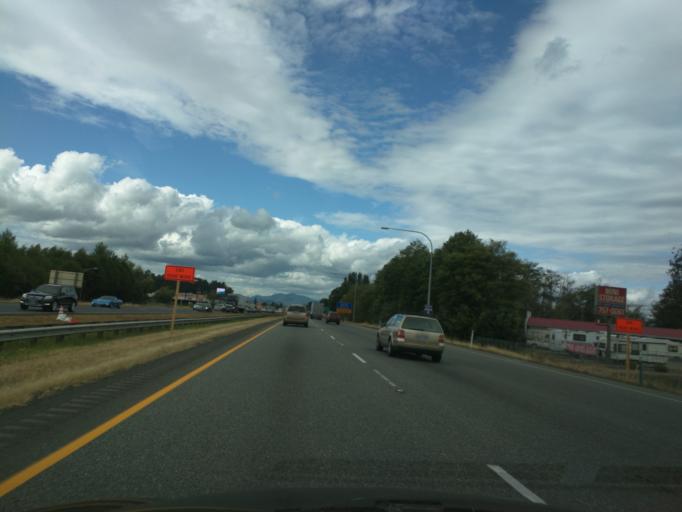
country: US
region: Washington
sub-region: Skagit County
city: Burlington
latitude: 48.4569
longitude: -122.3415
